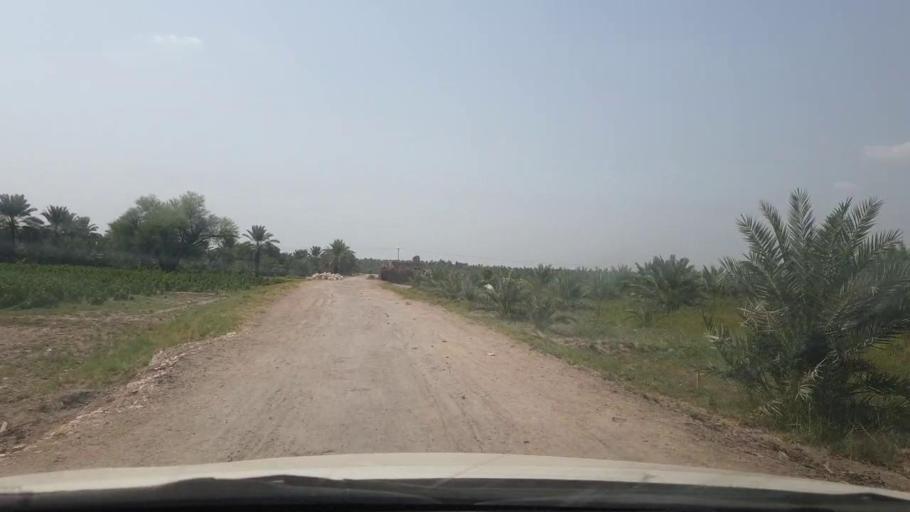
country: PK
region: Sindh
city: Khairpur
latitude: 27.5628
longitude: 68.8460
